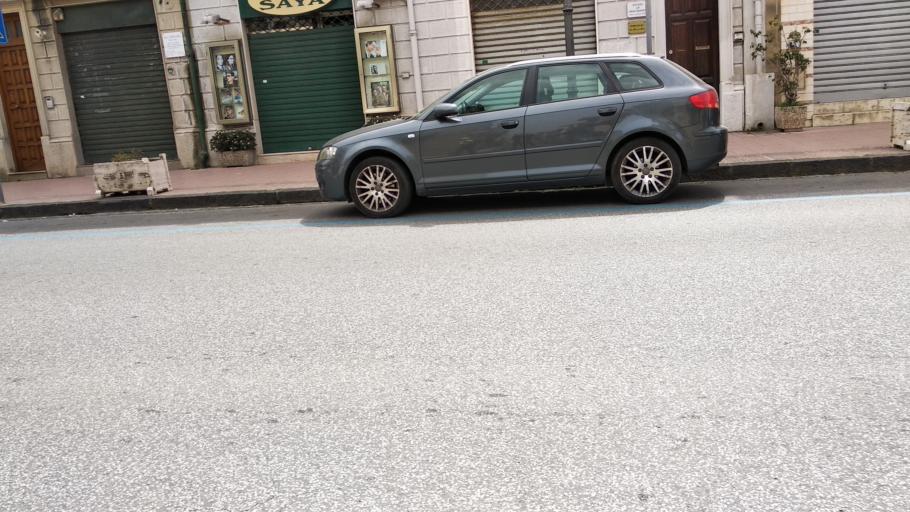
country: IT
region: Sicily
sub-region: Messina
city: Spadafora
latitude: 38.2217
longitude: 15.3766
